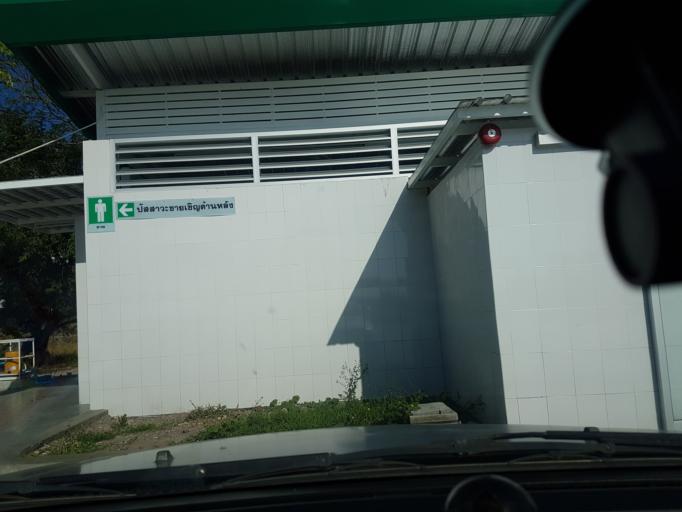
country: TH
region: Lop Buri
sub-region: Amphoe Tha Luang
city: Tha Luang
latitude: 15.0750
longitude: 100.9912
